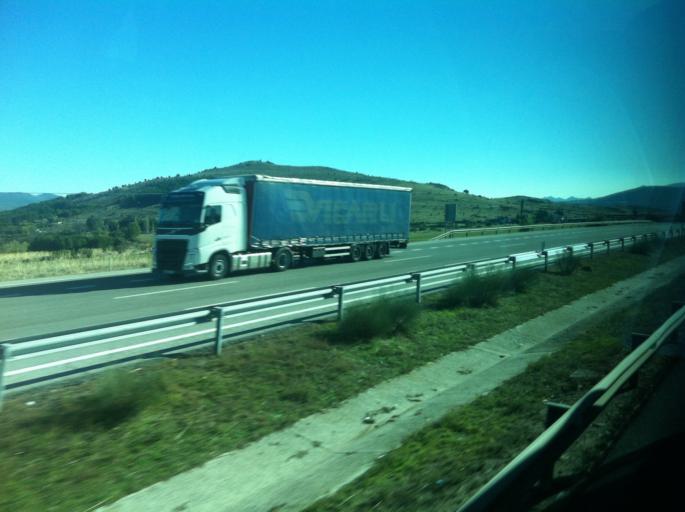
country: ES
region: Madrid
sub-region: Provincia de Madrid
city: Braojos
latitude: 41.0380
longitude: -3.6177
